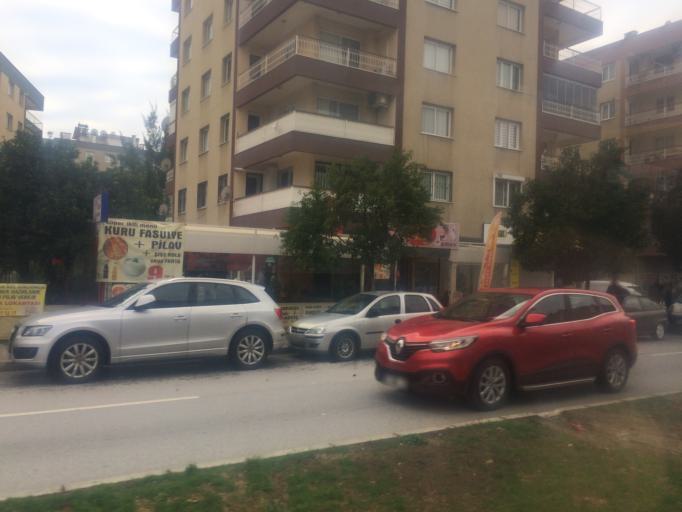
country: TR
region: Izmir
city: Karsiyaka
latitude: 38.4931
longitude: 27.0562
